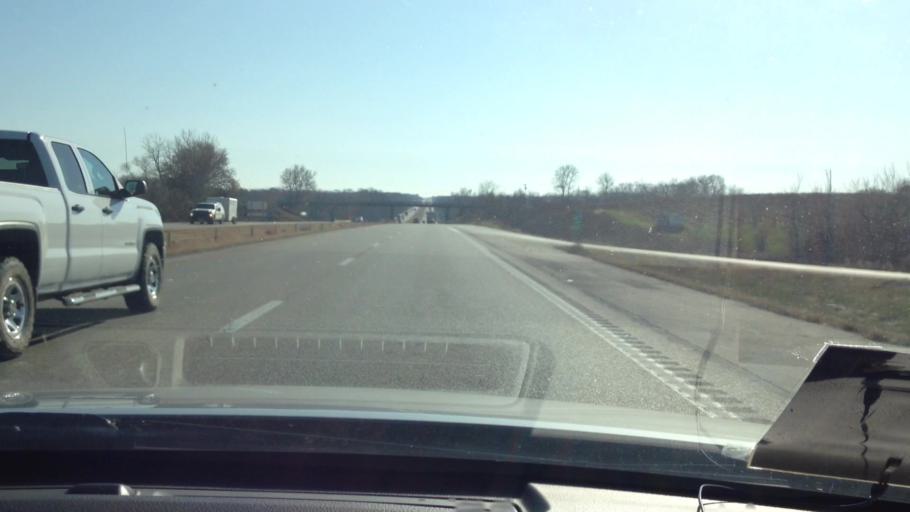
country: US
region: Missouri
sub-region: Platte County
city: Platte City
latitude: 39.4741
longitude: -94.7875
